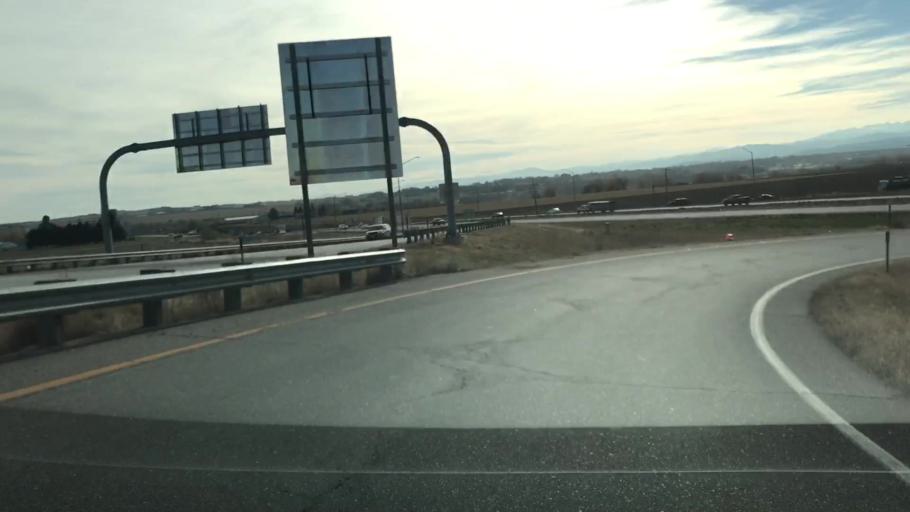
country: US
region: Colorado
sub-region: Larimer County
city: Loveland
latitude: 40.4063
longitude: -104.9918
